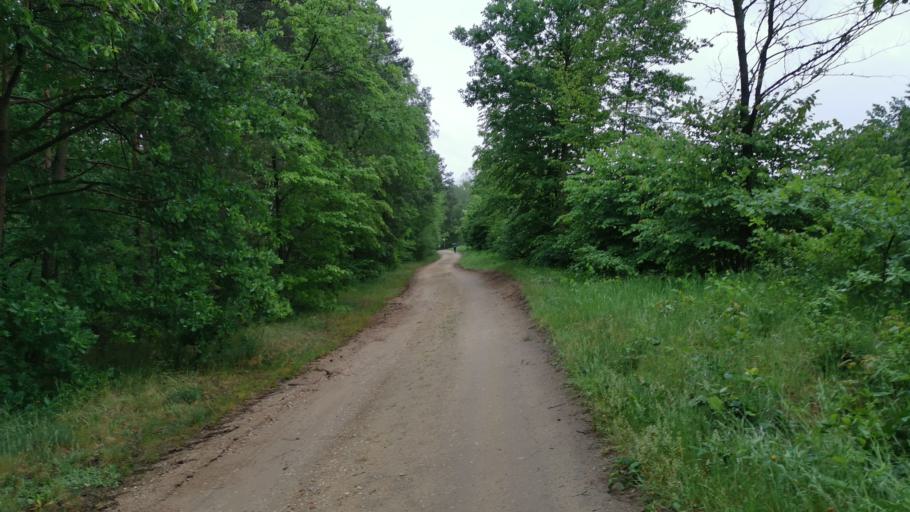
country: DE
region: Bavaria
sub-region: Regierungsbezirk Mittelfranken
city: Roth
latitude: 49.2536
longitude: 11.1116
